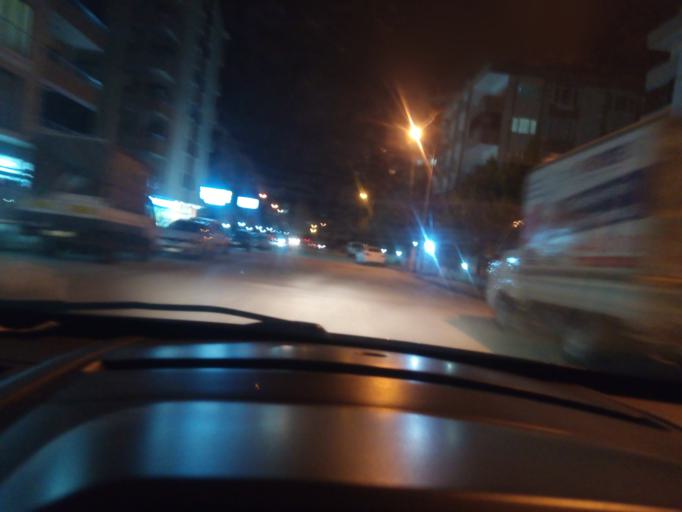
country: TR
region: Bursa
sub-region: Mudanya
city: Mudanya
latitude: 40.3532
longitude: 28.9175
